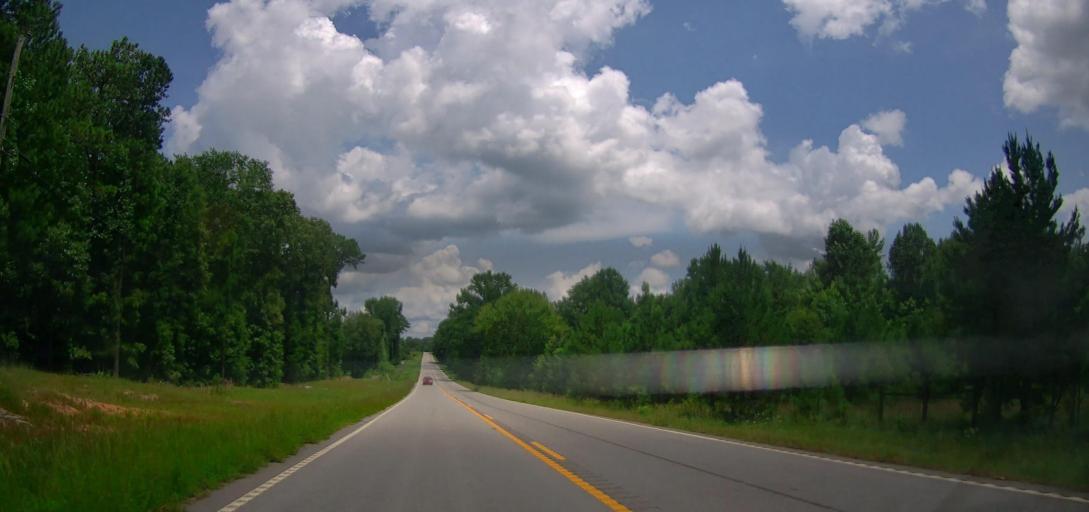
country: US
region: Georgia
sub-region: Meriwether County
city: Greenville
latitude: 33.0103
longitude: -84.6583
